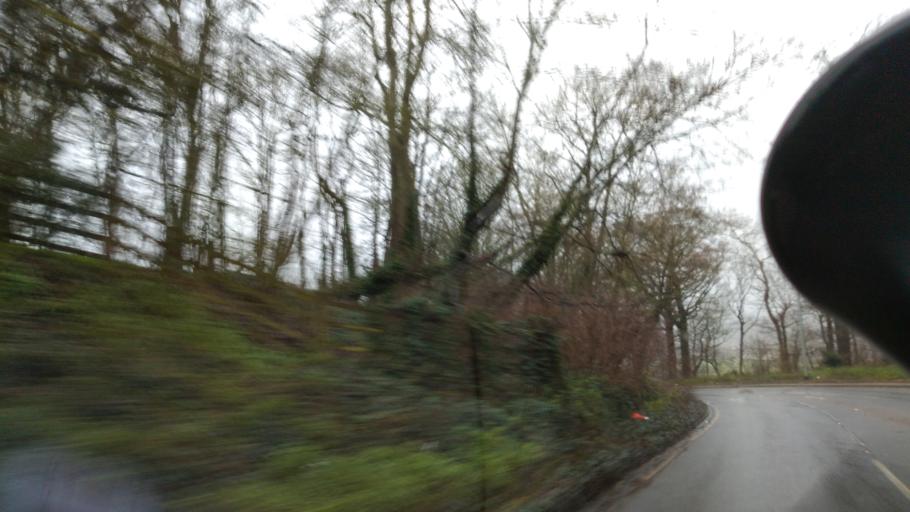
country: GB
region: England
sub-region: West Sussex
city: Arundel
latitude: 50.8466
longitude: -0.5412
